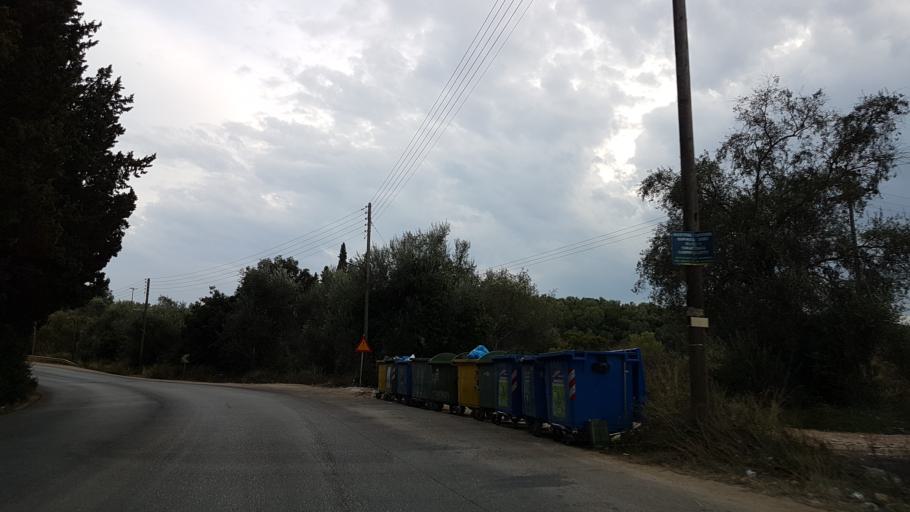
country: GR
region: Ionian Islands
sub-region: Nomos Kerkyras
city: Kontokali
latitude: 39.6718
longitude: 19.8396
